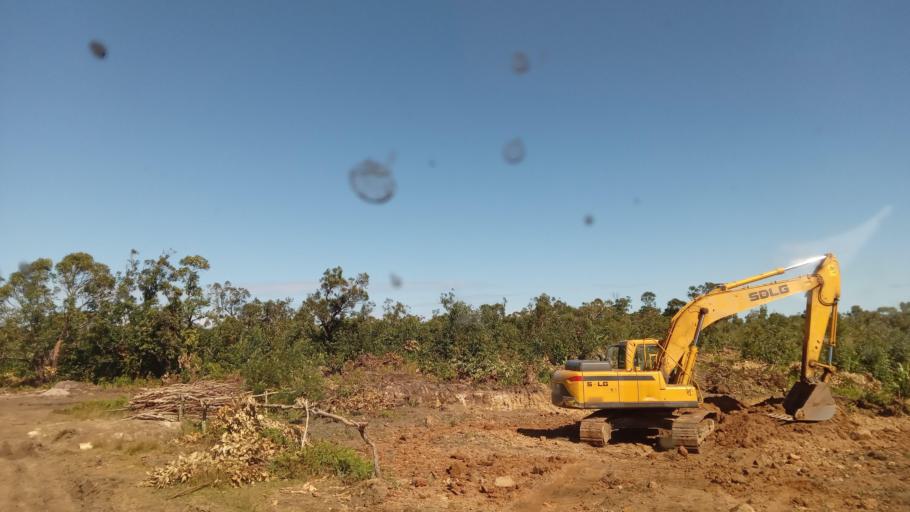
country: MG
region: Atsimo-Atsinanana
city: Vohipaho
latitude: -23.6160
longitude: 47.6030
